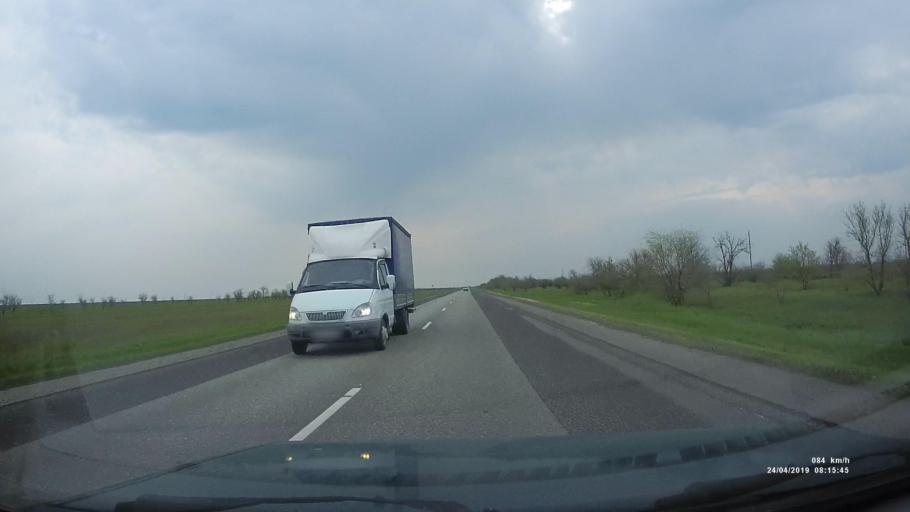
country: RU
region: Kalmykiya
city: Priyutnoye
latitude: 46.0997
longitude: 43.6001
